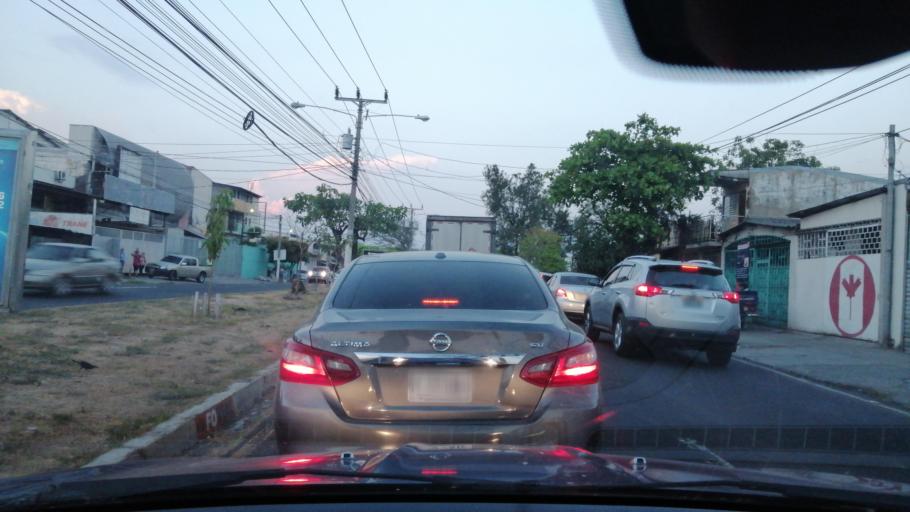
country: SV
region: San Salvador
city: Mejicanos
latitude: 13.7265
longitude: -89.2209
